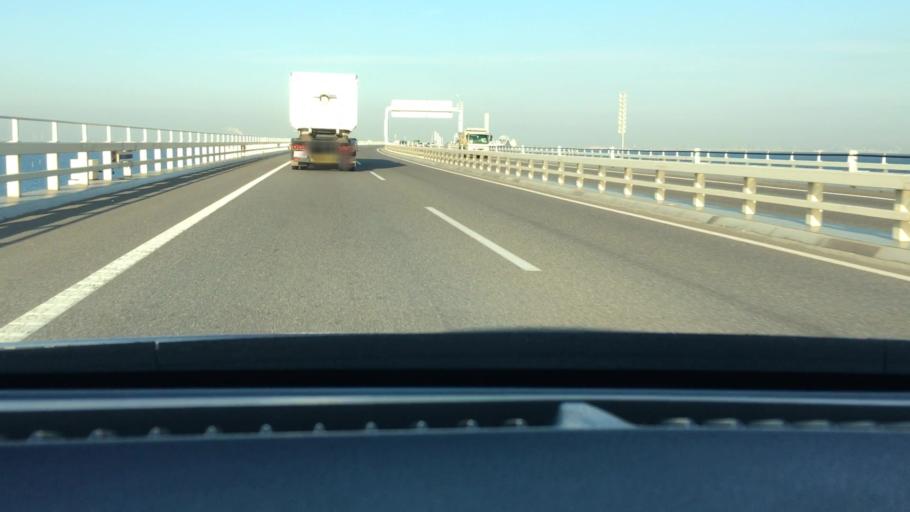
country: JP
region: Chiba
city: Kisarazu
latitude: 35.4374
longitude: 139.9146
